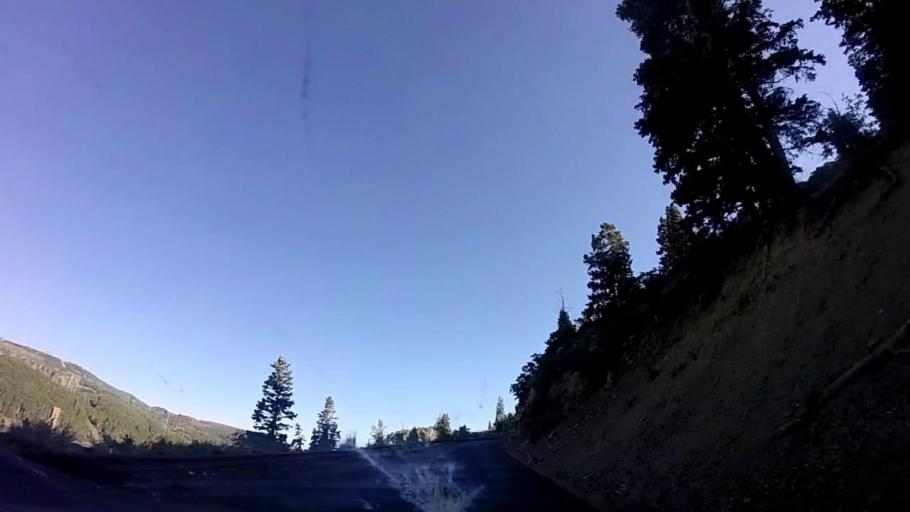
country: US
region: Utah
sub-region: Summit County
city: Park City
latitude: 40.6216
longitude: -111.4930
